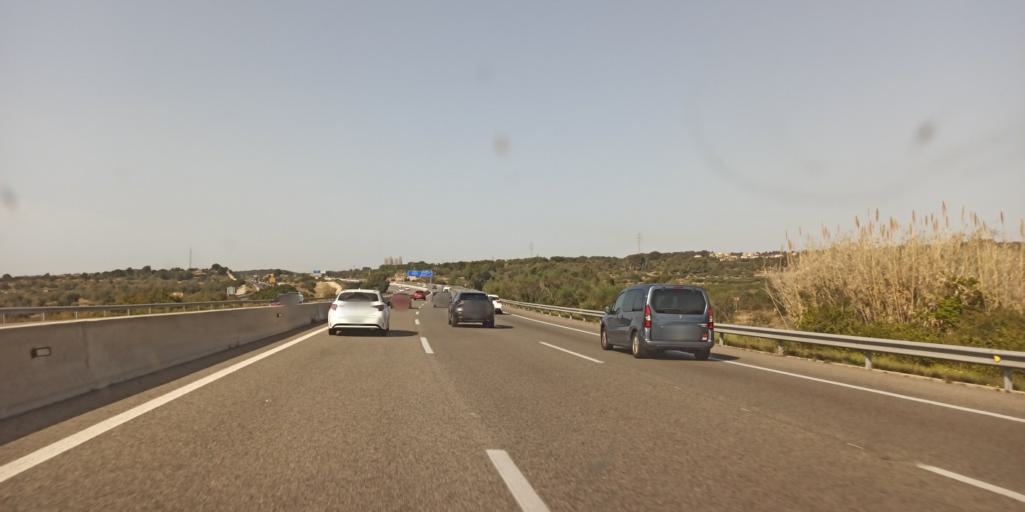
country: ES
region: Catalonia
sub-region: Provincia de Tarragona
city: Torredembarra
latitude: 41.1633
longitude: 1.4092
